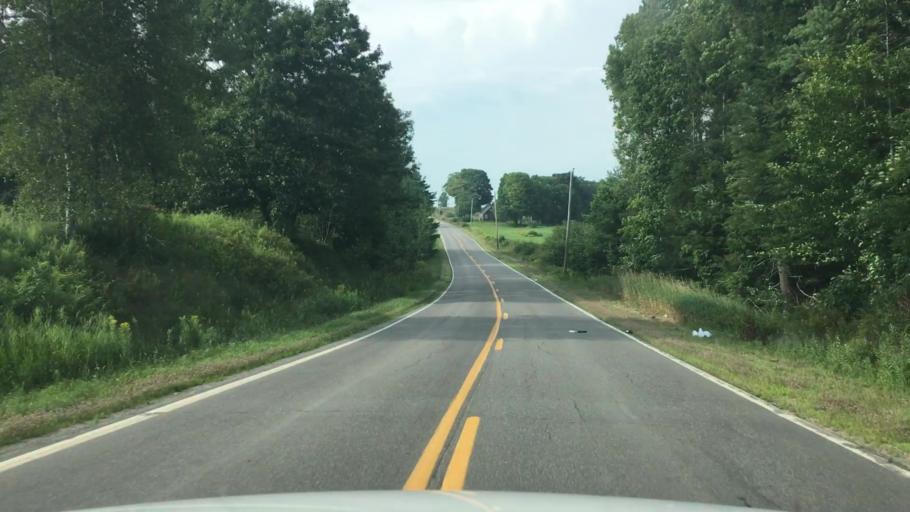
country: US
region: Maine
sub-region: Knox County
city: Washington
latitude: 44.2098
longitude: -69.3829
